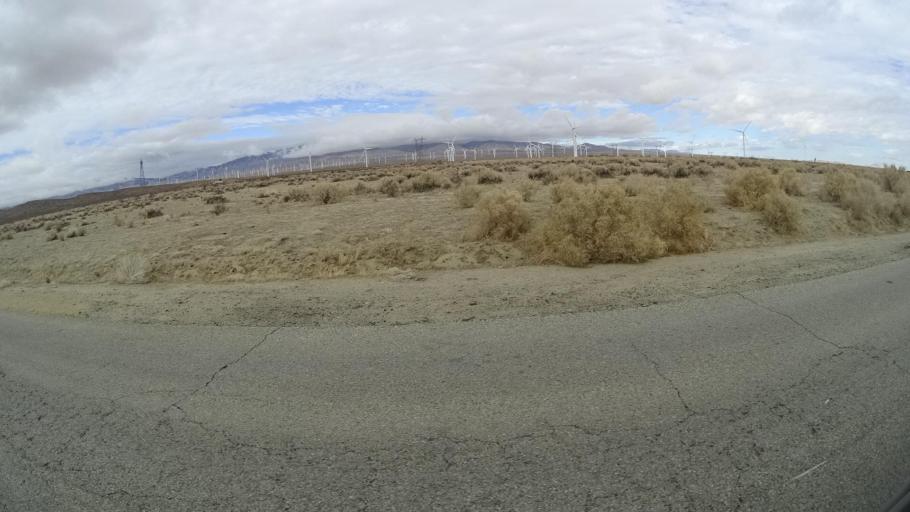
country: US
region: California
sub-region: Los Angeles County
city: Green Valley
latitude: 34.8627
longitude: -118.4243
